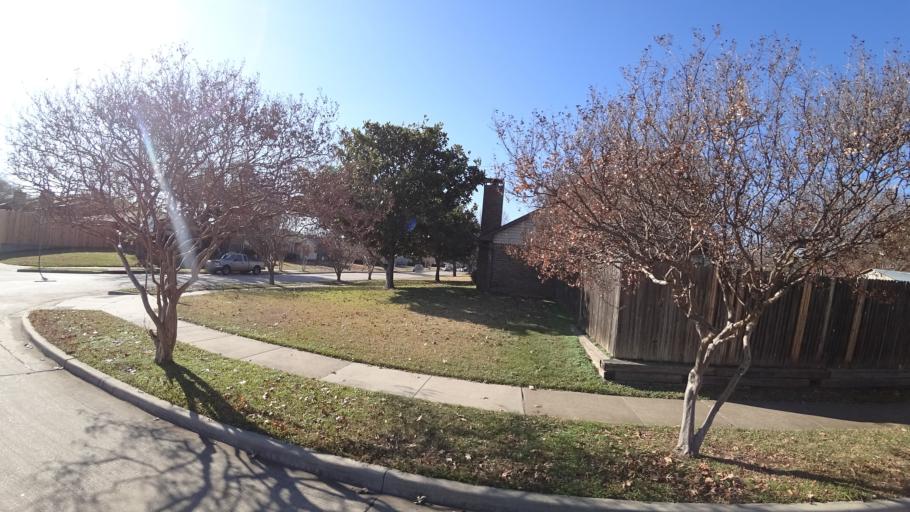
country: US
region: Texas
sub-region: Denton County
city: Lewisville
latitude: 33.0075
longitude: -96.9973
